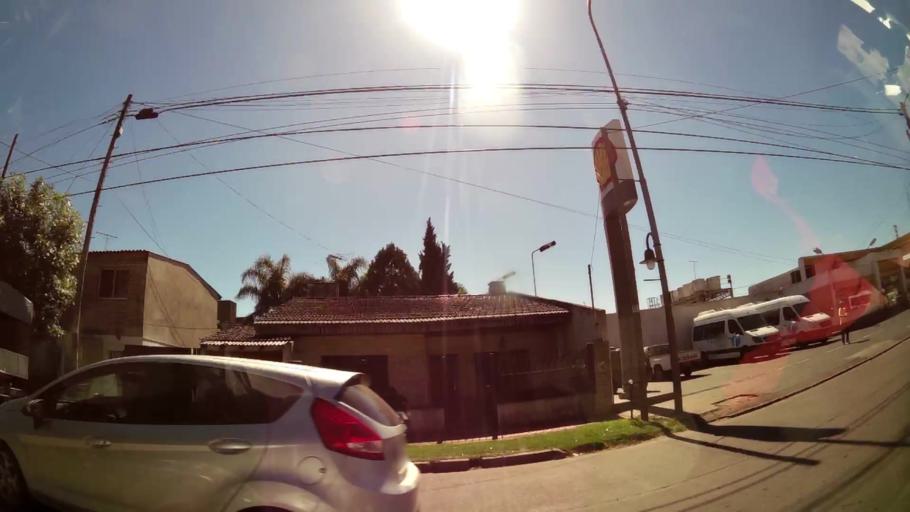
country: AR
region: Buenos Aires
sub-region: Partido de Tigre
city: Tigre
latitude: -34.4870
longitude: -58.6196
